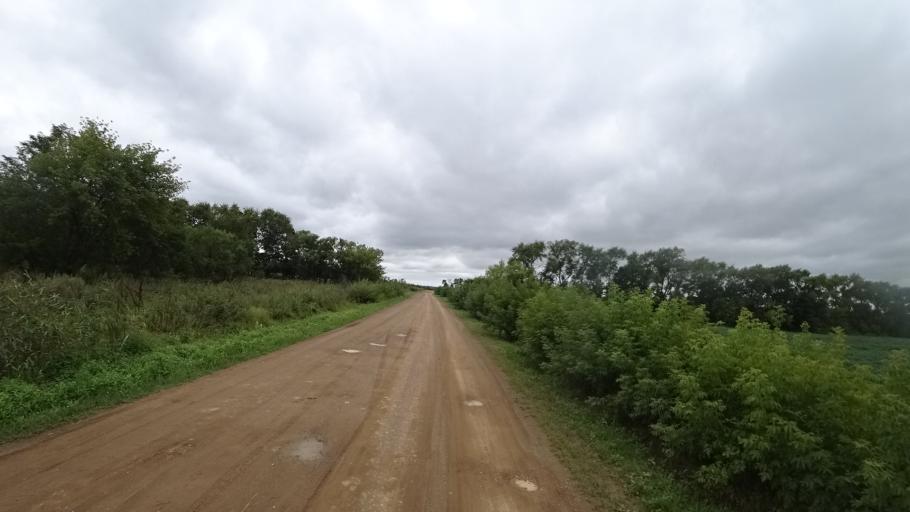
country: RU
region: Primorskiy
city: Chernigovka
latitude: 44.4523
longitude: 132.5794
